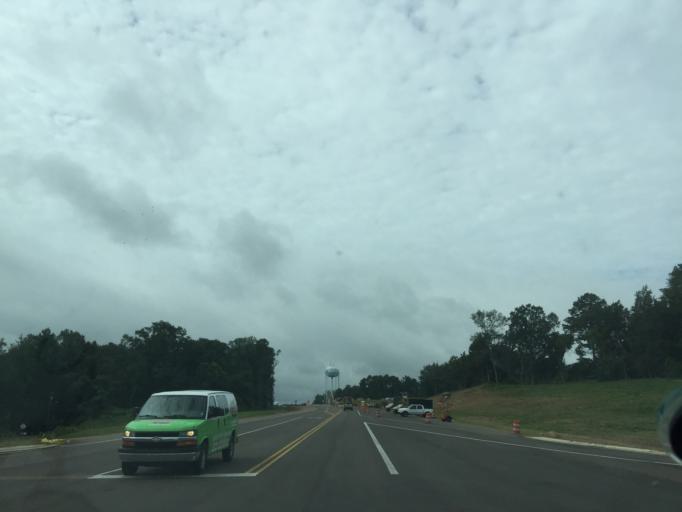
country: US
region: Mississippi
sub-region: Rankin County
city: Brandon
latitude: 32.2838
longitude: -89.9927
